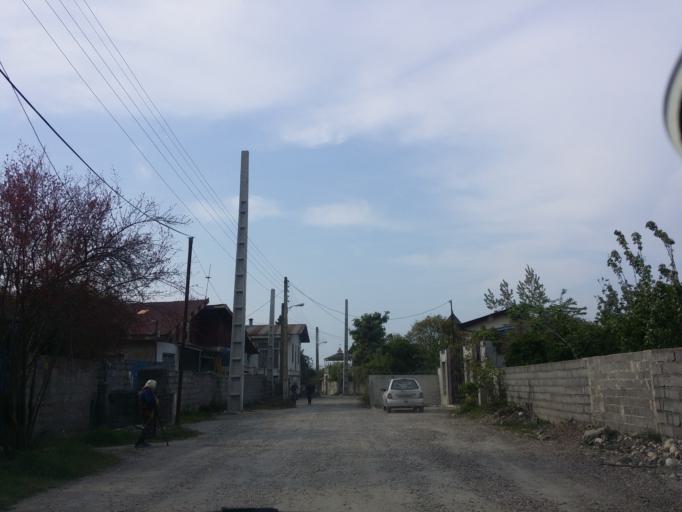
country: IR
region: Mazandaran
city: Chalus
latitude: 36.6789
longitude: 51.3932
